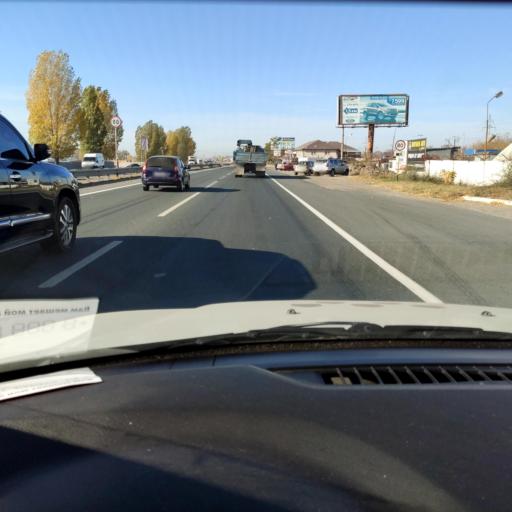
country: RU
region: Samara
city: Tol'yatti
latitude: 53.5716
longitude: 49.4677
